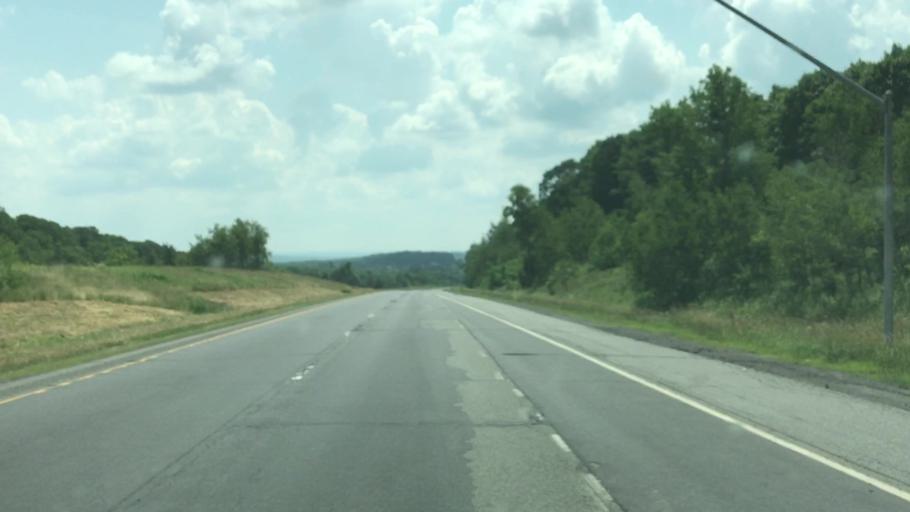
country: US
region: Pennsylvania
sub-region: Lackawanna County
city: Mount Cobb
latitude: 41.4044
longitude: -75.4982
